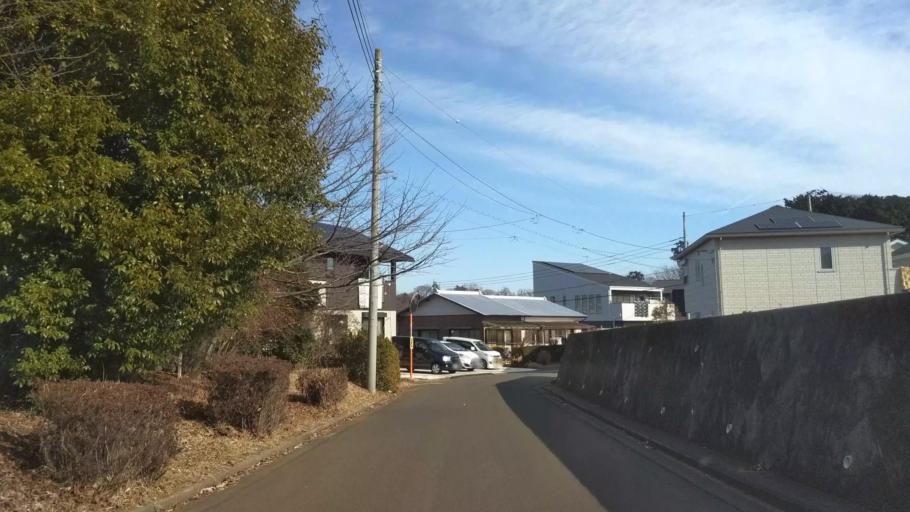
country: JP
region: Kanagawa
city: Hadano
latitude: 35.3606
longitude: 139.2328
